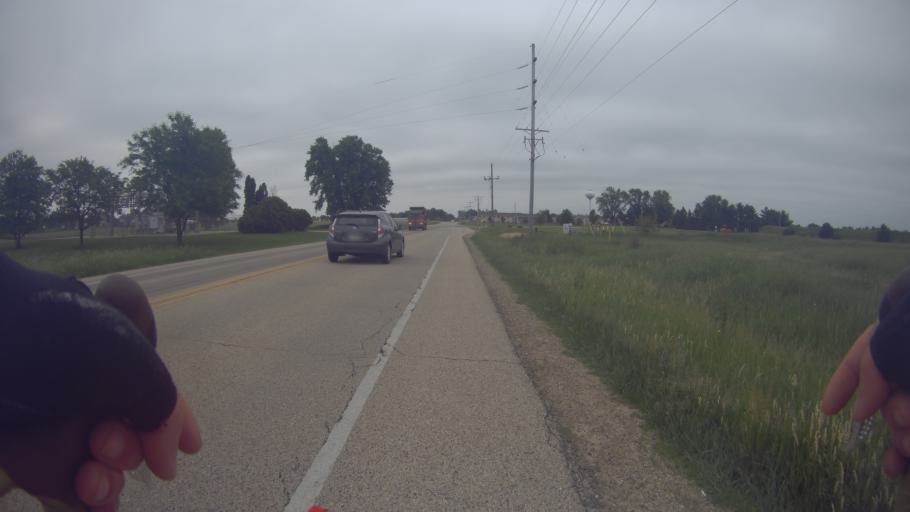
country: US
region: Wisconsin
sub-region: Green County
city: Brooklyn
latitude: 42.8640
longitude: -89.3692
